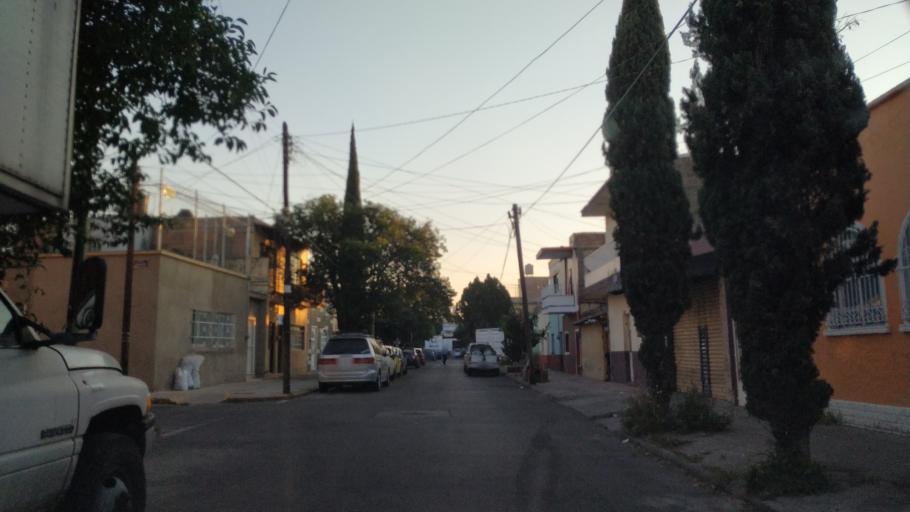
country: MX
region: Jalisco
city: Tlaquepaque
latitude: 20.6566
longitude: -103.3319
